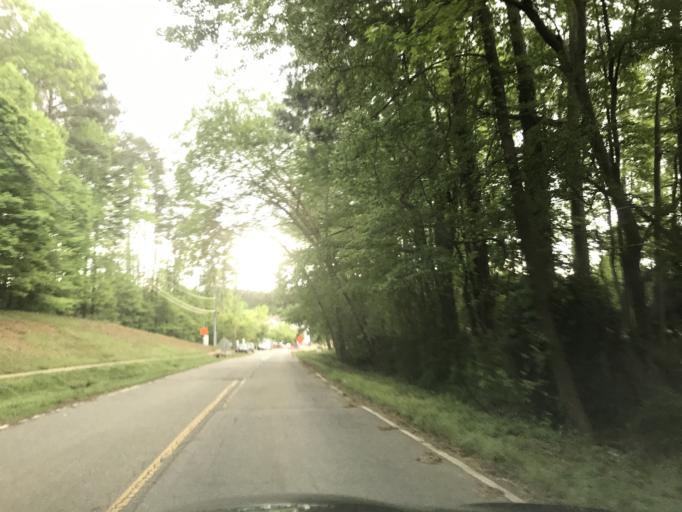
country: US
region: North Carolina
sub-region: Wake County
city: West Raleigh
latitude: 35.7648
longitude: -78.7044
